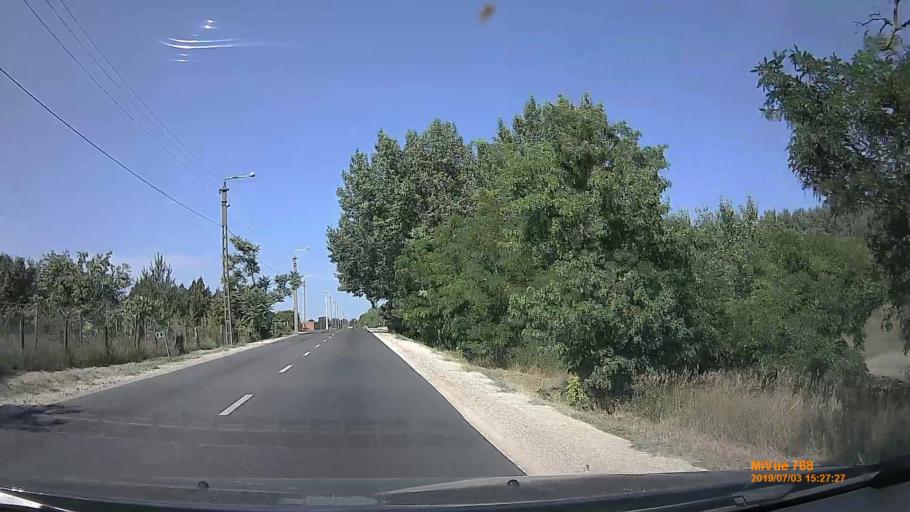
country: HU
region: Gyor-Moson-Sopron
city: Gyor
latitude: 47.7208
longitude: 17.6577
